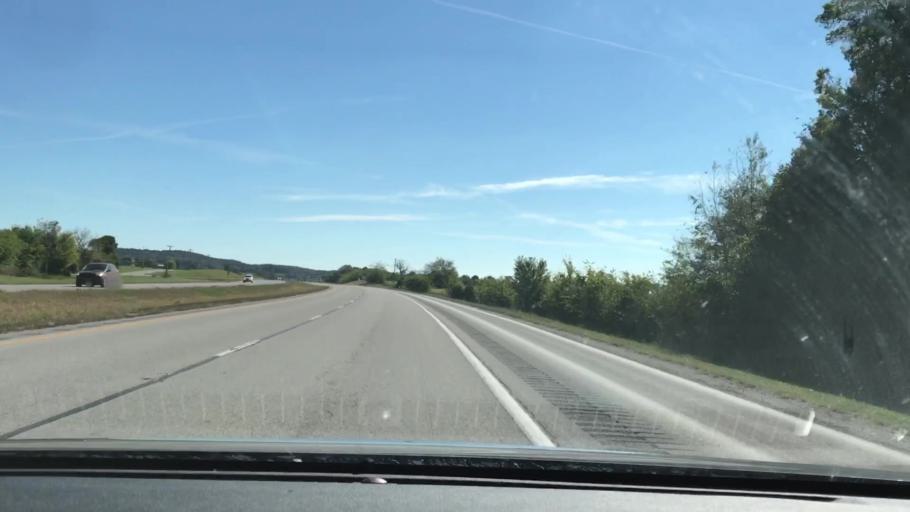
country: US
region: Kentucky
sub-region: Todd County
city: Elkton
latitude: 36.8421
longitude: -87.2640
